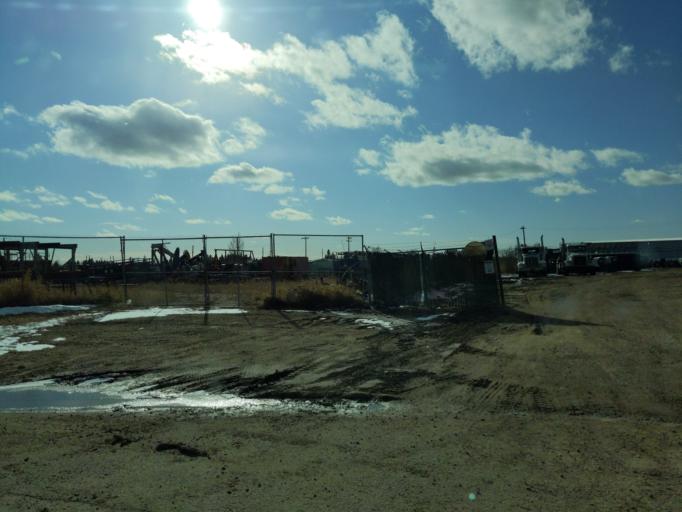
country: CA
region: Saskatchewan
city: Lloydminster
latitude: 53.2838
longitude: -109.9836
